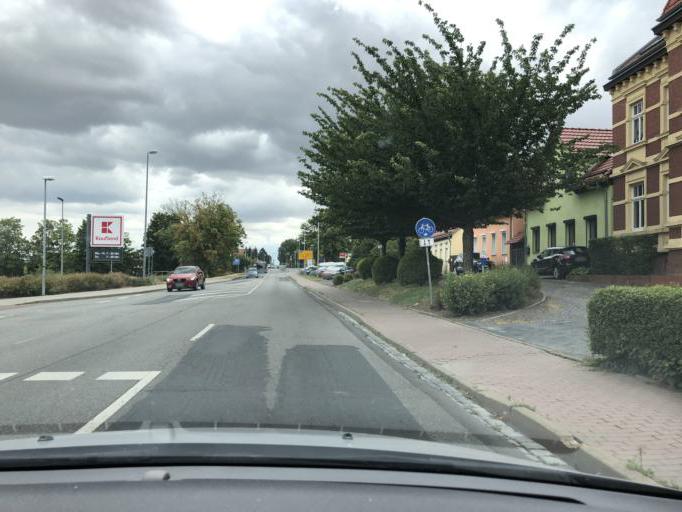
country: DE
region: Saxony-Anhalt
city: Volkstedt
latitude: 51.5232
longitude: 11.5561
